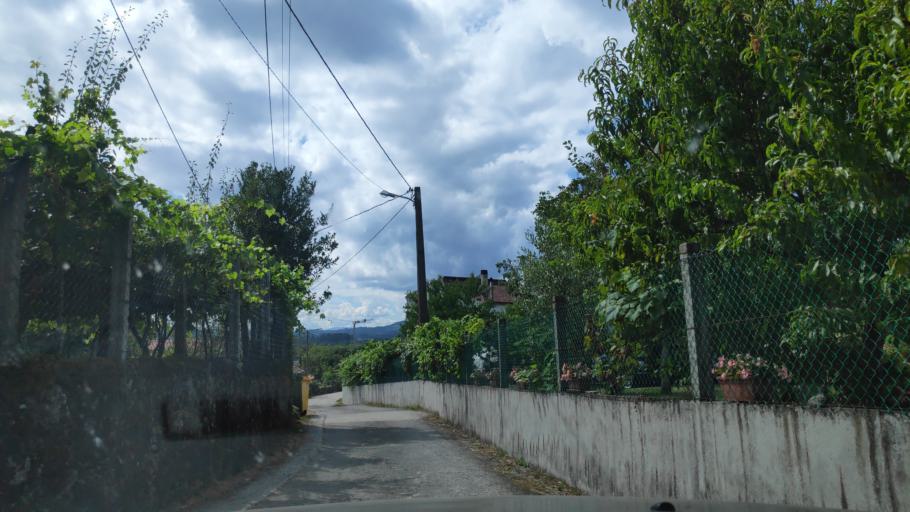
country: ES
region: Galicia
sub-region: Provincia da Coruna
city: Padron
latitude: 42.7299
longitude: -8.6737
